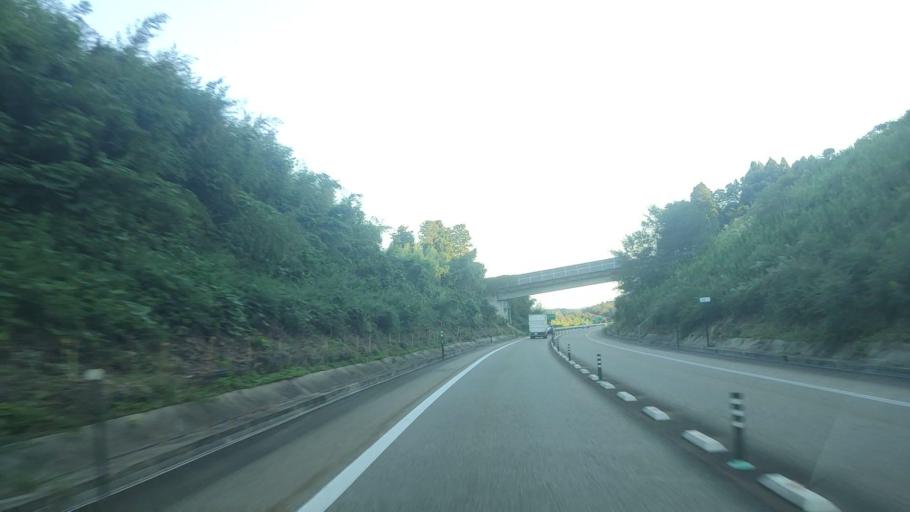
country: JP
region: Ishikawa
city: Nanao
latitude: 36.9927
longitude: 137.0463
